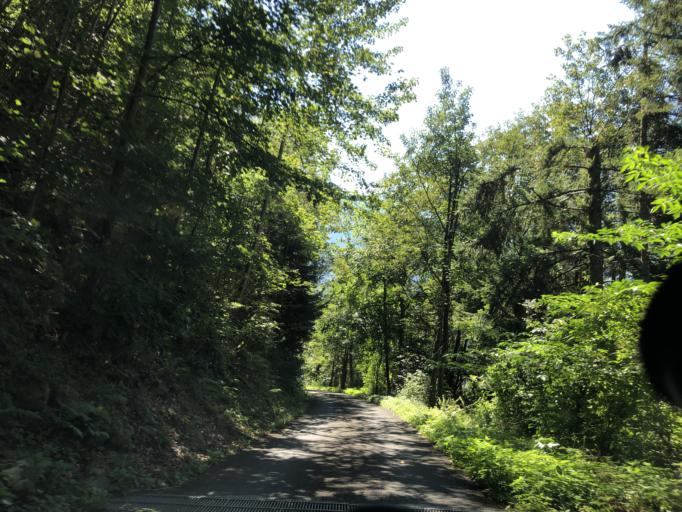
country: CH
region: Uri
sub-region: Uri
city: Flueelen
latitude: 46.9034
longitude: 8.6329
